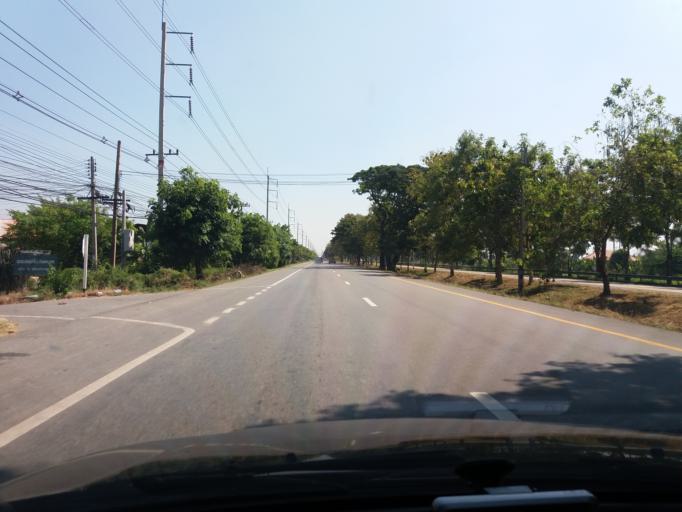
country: TH
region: Chai Nat
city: Sankhaburi
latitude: 15.0780
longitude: 100.1433
